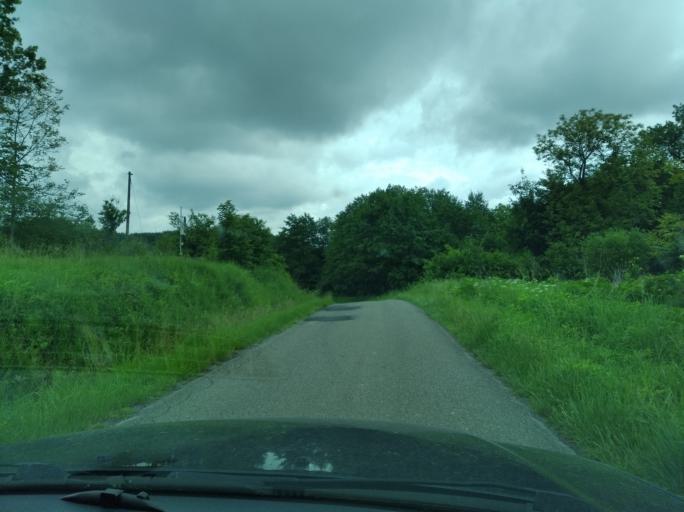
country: PL
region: Subcarpathian Voivodeship
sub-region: Powiat przemyski
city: Nienadowa
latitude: 49.8595
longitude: 22.4104
